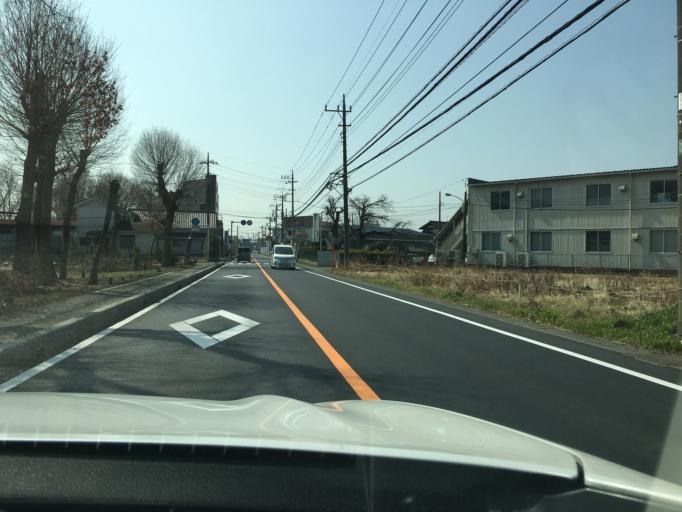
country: JP
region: Saitama
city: Kamifukuoka
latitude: 35.8503
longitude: 139.4677
